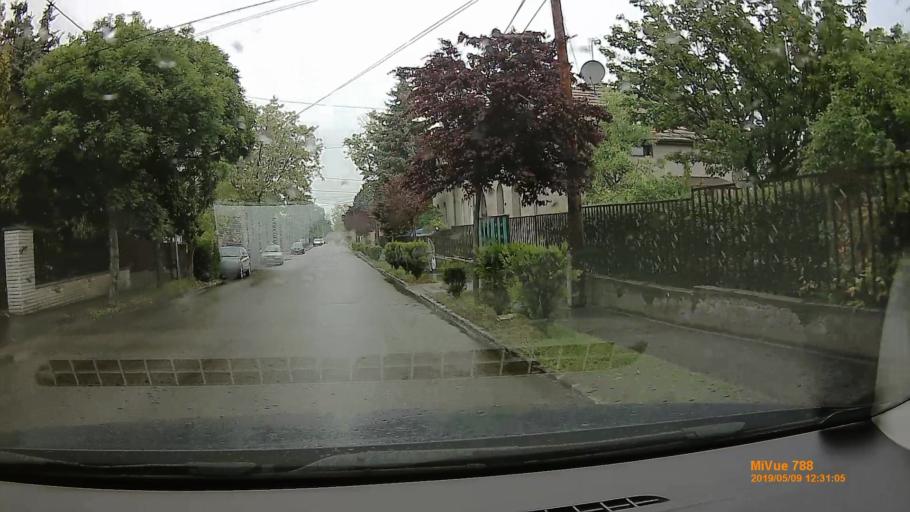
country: HU
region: Budapest
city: Budapest XVI. keruelet
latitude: 47.5217
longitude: 19.1737
